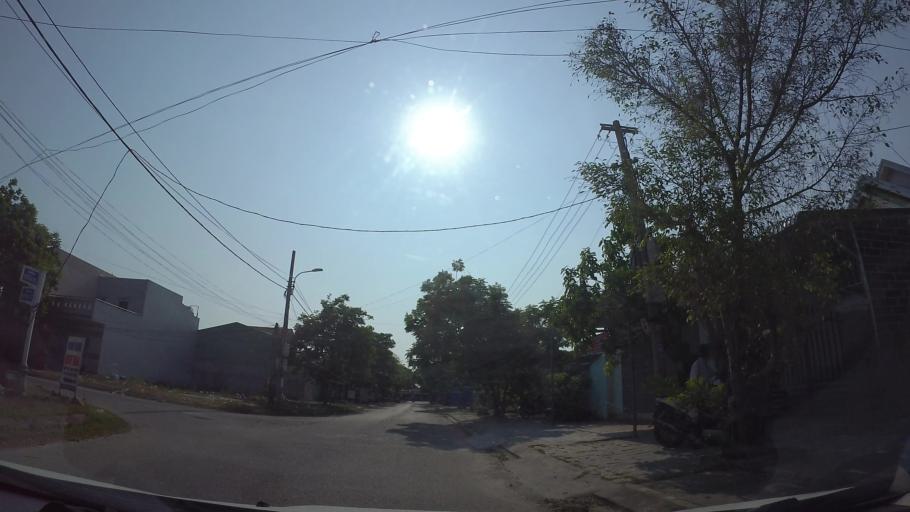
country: VN
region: Da Nang
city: Ngu Hanh Son
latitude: 15.9542
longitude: 108.2593
